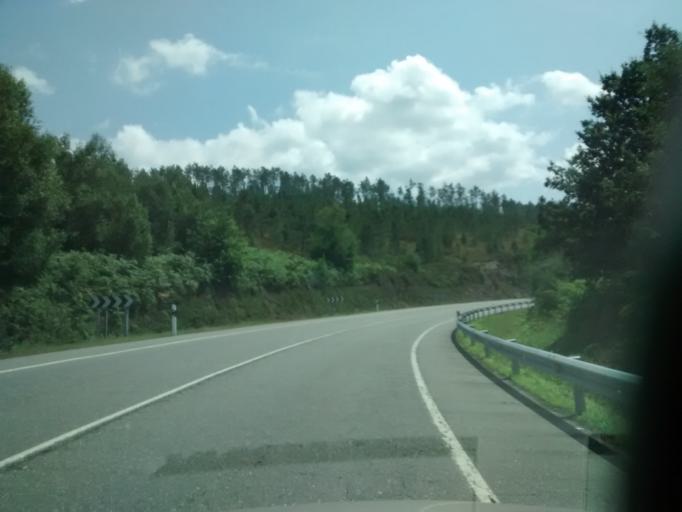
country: ES
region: Galicia
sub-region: Provincia de Pontevedra
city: Forcarei
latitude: 42.5430
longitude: -8.3426
